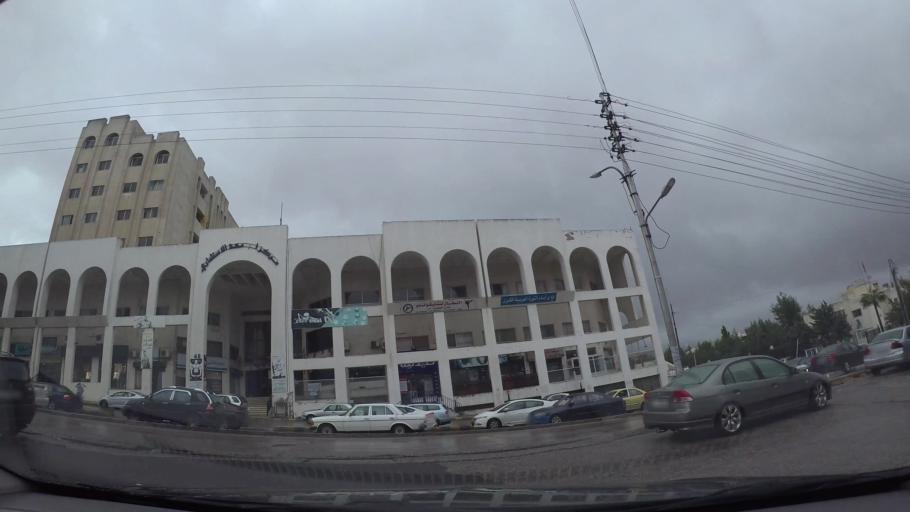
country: JO
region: Amman
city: Al Jubayhah
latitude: 32.0224
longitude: 35.8727
